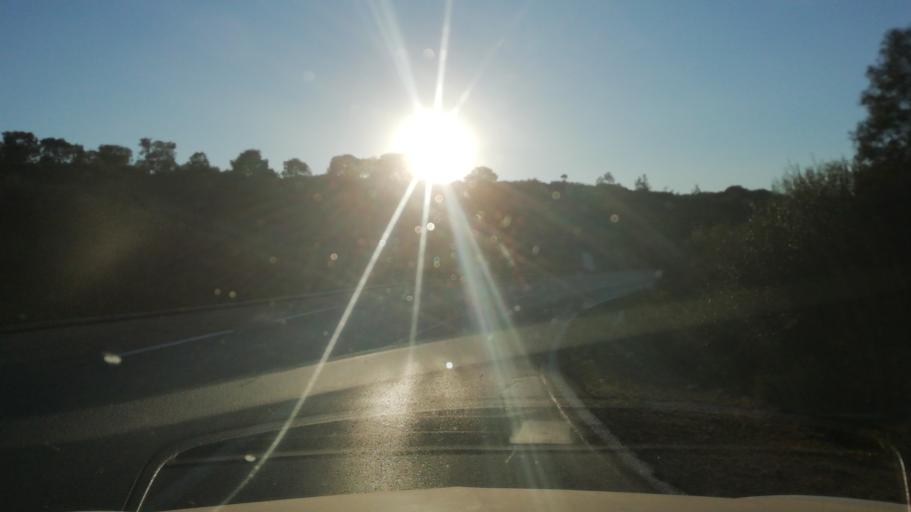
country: DZ
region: Tlemcen
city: Beni Mester
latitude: 34.8127
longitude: -1.6240
